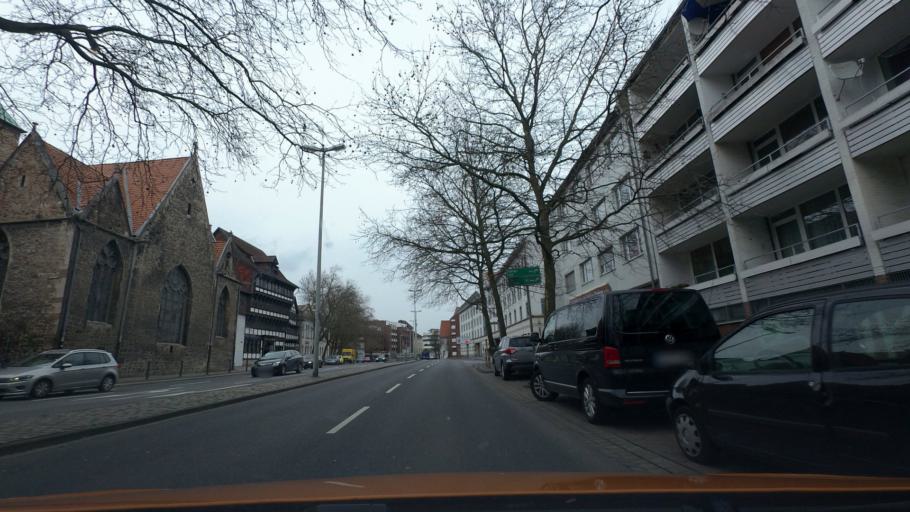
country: DE
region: Lower Saxony
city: Braunschweig
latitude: 52.2604
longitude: 10.5156
